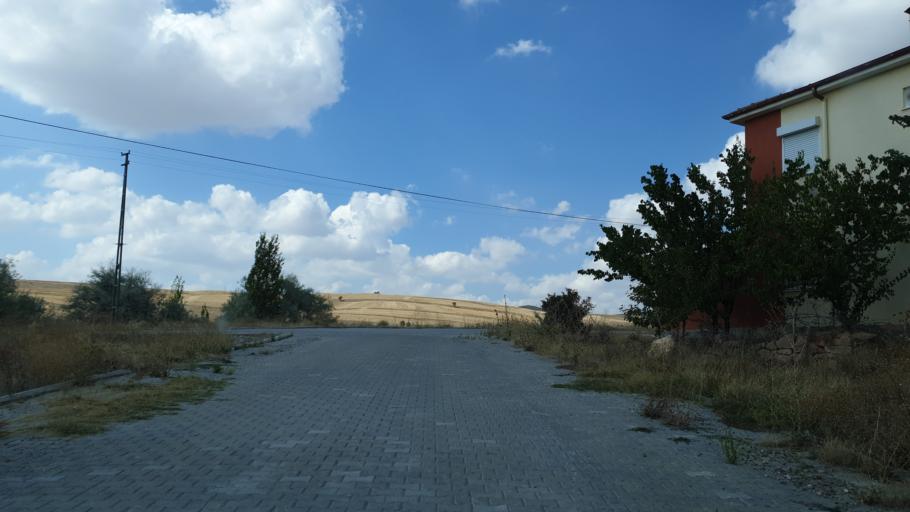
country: TR
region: Kayseri
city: Felahiye
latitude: 39.1174
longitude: 35.6079
